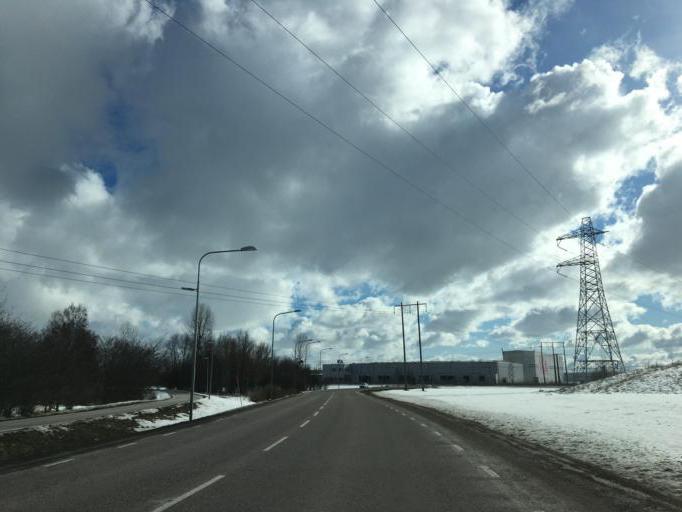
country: SE
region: Vaestmanland
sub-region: Vasteras
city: Vasteras
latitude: 59.5925
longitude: 16.4679
